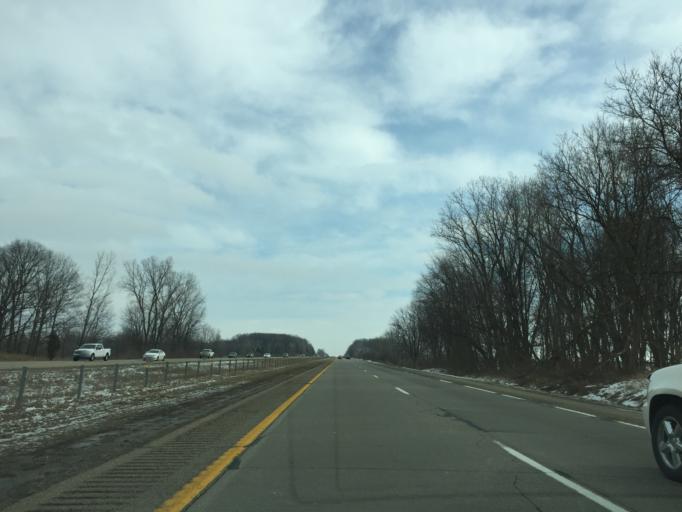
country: US
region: Michigan
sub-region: Kent County
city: Forest Hills
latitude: 42.8782
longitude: -85.4466
